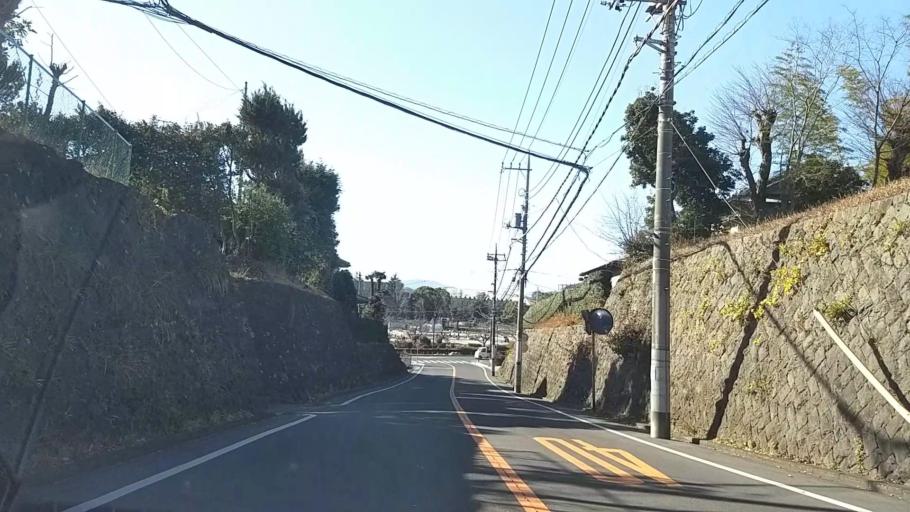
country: JP
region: Kanagawa
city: Hadano
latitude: 35.3819
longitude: 139.2043
